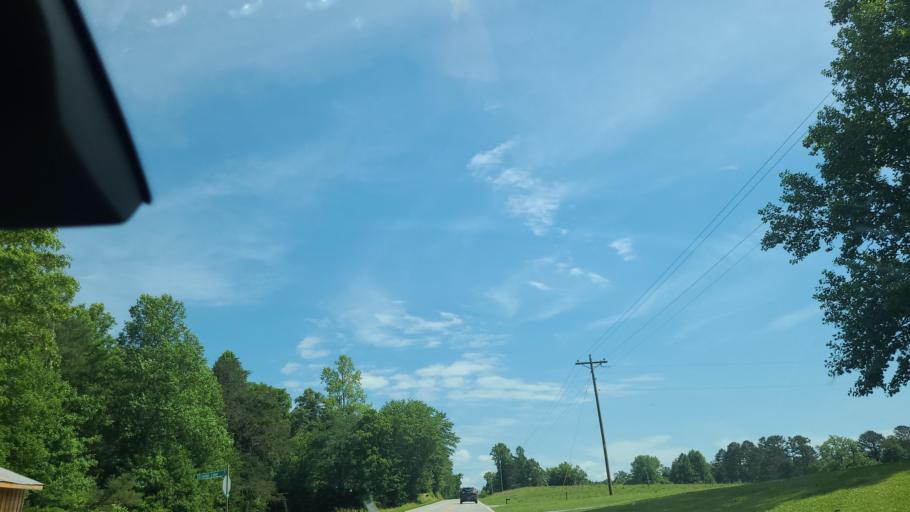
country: US
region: South Carolina
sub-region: Oconee County
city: Walhalla
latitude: 34.8326
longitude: -83.1318
